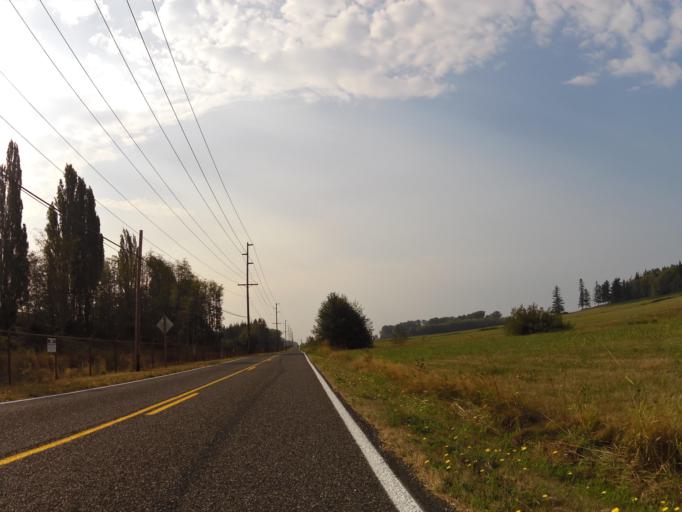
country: US
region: Washington
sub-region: Whatcom County
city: Birch Bay
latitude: 48.8844
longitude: -122.7488
